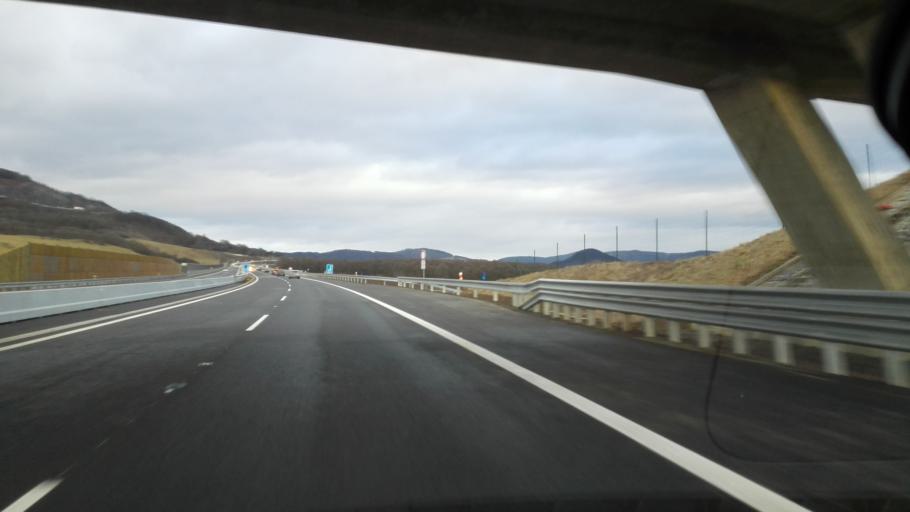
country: CZ
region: Ustecky
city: Velemin
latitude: 50.5514
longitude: 14.0118
